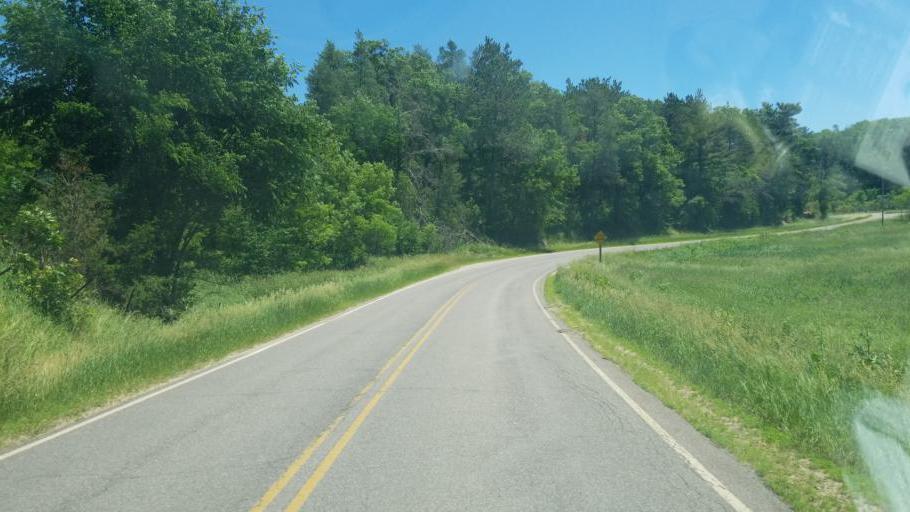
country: US
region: Wisconsin
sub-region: Juneau County
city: Elroy
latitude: 43.7873
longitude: -90.2780
